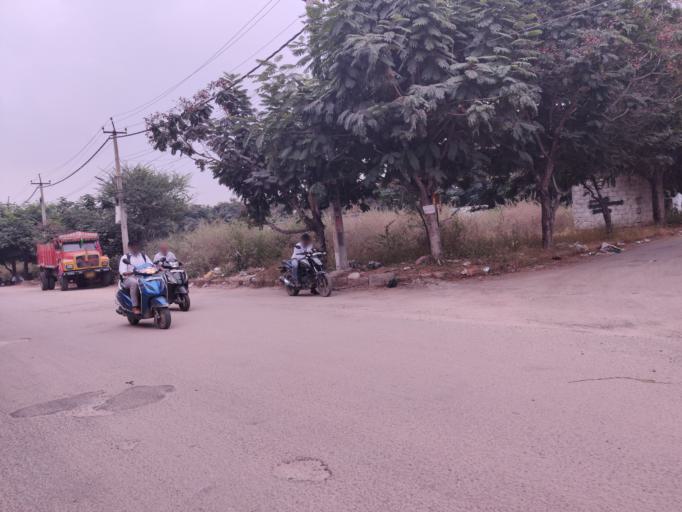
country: IN
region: Telangana
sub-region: Hyderabad
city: Hyderabad
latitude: 17.4071
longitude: 78.3948
